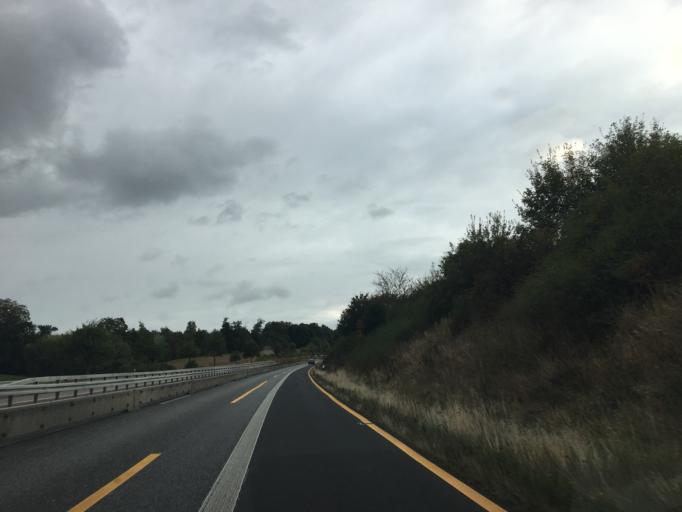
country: DE
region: Hesse
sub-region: Regierungsbezirk Giessen
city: Fronhausen
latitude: 50.6982
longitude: 8.7304
